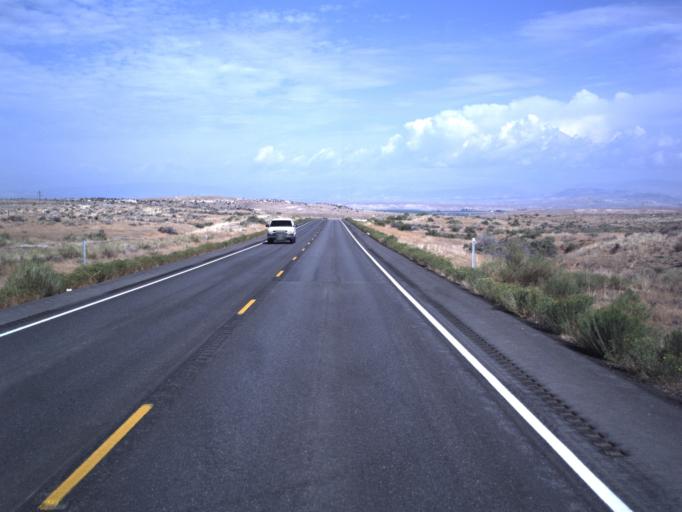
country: US
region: Utah
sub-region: Uintah County
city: Naples
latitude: 40.3377
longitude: -109.2919
